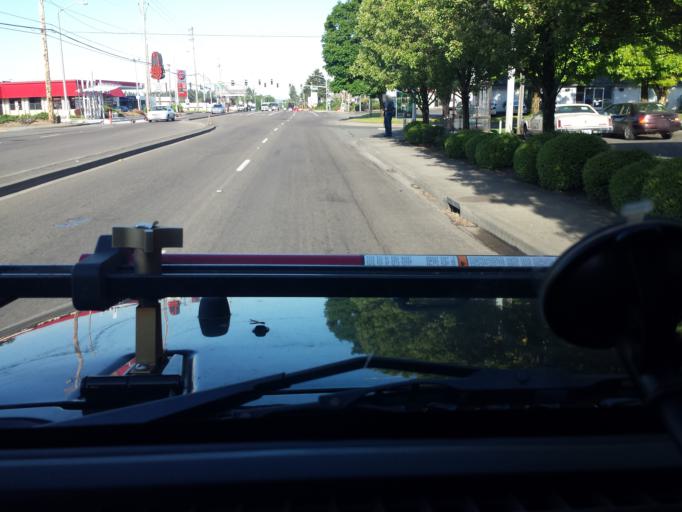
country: US
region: Washington
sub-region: Clark County
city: Walnut Grove
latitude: 45.6452
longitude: -122.5987
